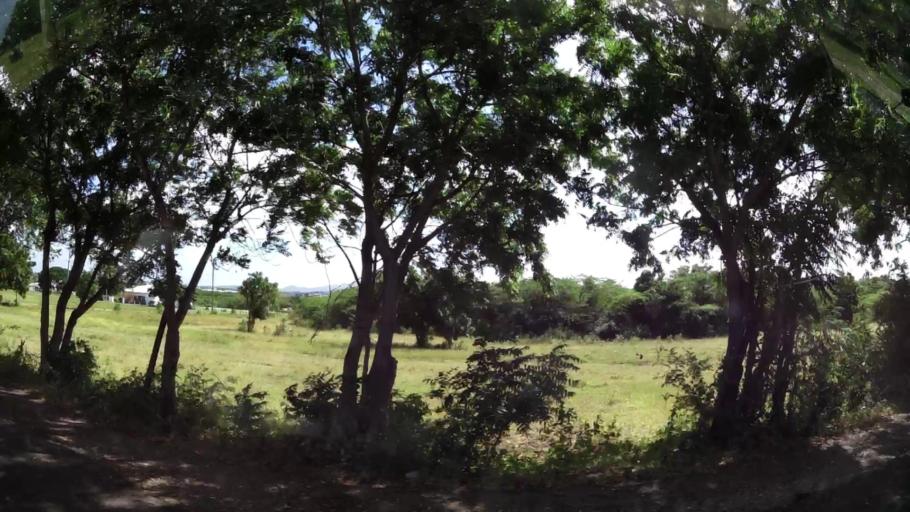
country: AG
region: Saint John
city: Saint John's
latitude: 17.1355
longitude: -61.8582
